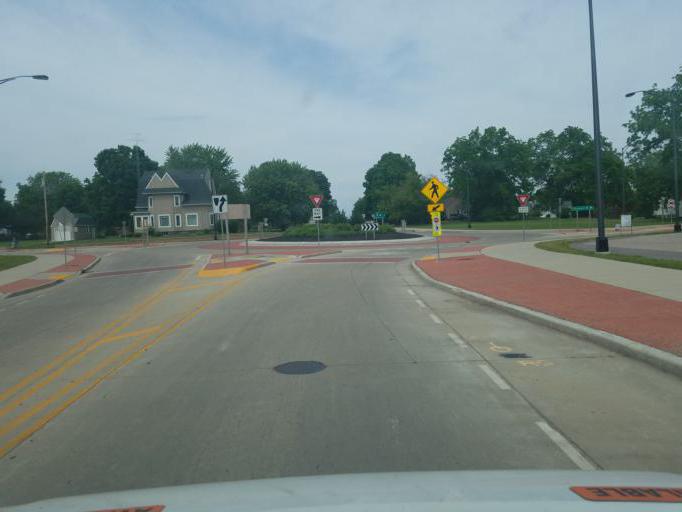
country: US
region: Wisconsin
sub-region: Juneau County
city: Mauston
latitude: 43.7891
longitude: -90.0760
